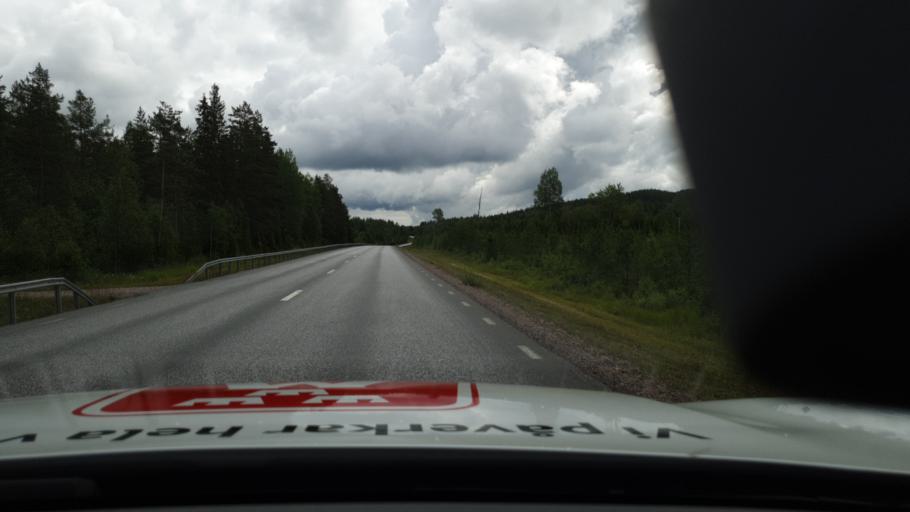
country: SE
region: Norrbotten
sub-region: Pitea Kommun
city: Norrfjarden
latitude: 65.6071
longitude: 21.4682
